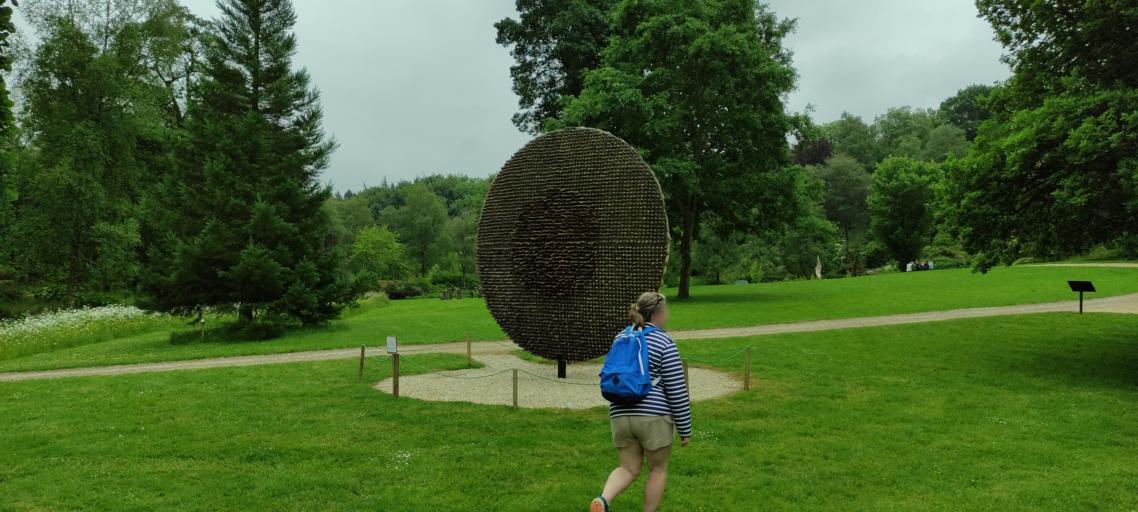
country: GB
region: England
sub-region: North Yorkshire
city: Bedale
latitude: 54.1928
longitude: -1.6742
